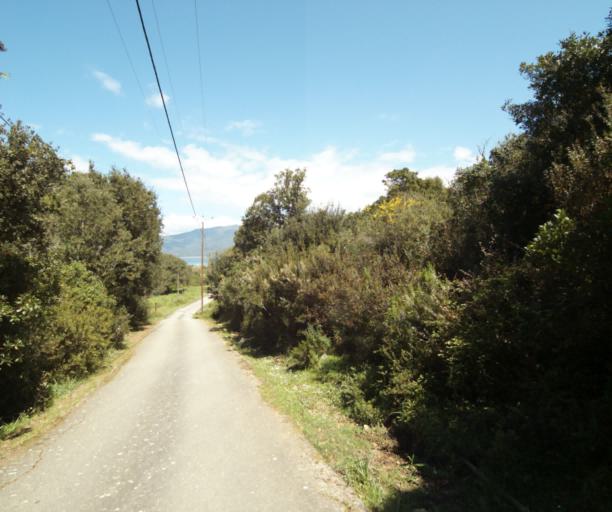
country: FR
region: Corsica
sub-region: Departement de la Corse-du-Sud
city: Propriano
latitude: 41.6402
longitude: 8.8688
